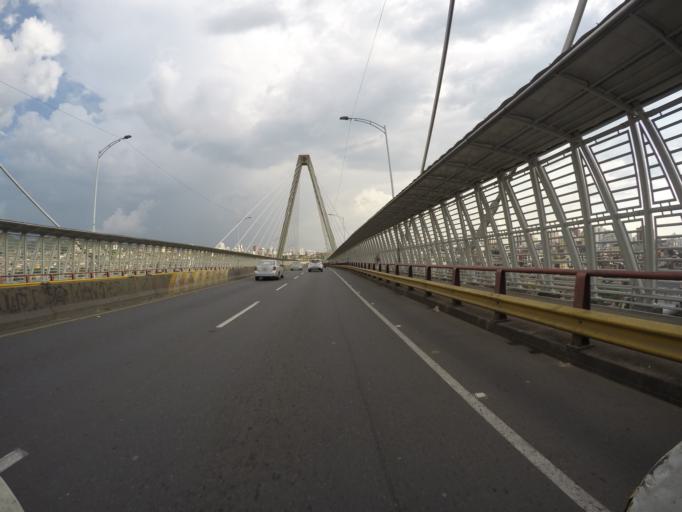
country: CO
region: Risaralda
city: Pereira
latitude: 4.8174
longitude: -75.6872
